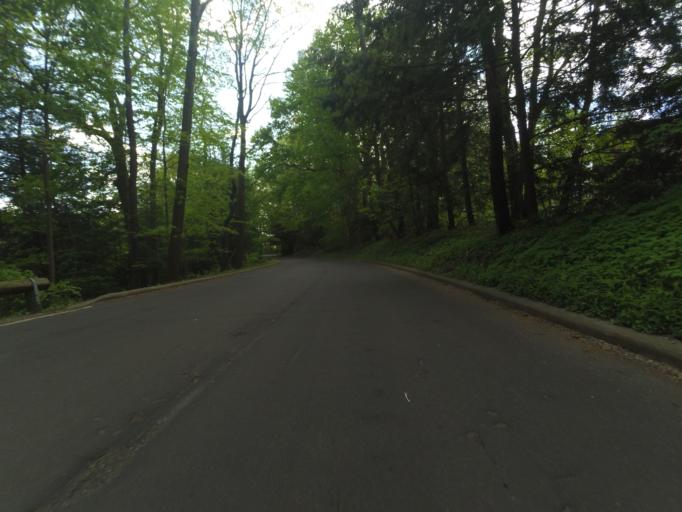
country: US
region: Ohio
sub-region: Mahoning County
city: Youngstown
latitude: 41.0825
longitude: -80.6812
